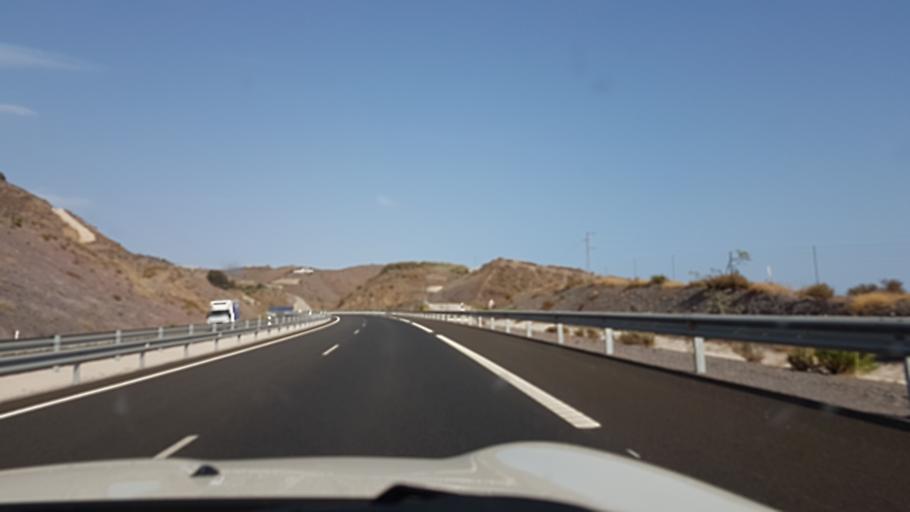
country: ES
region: Andalusia
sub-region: Provincia de Granada
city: Albunol
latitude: 36.7557
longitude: -3.2306
